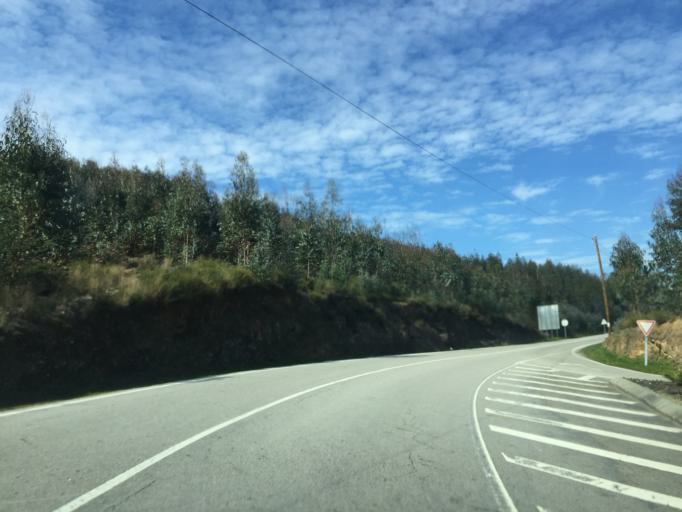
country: PT
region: Aveiro
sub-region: Arouca
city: Arouca
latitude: 40.9575
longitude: -8.1989
